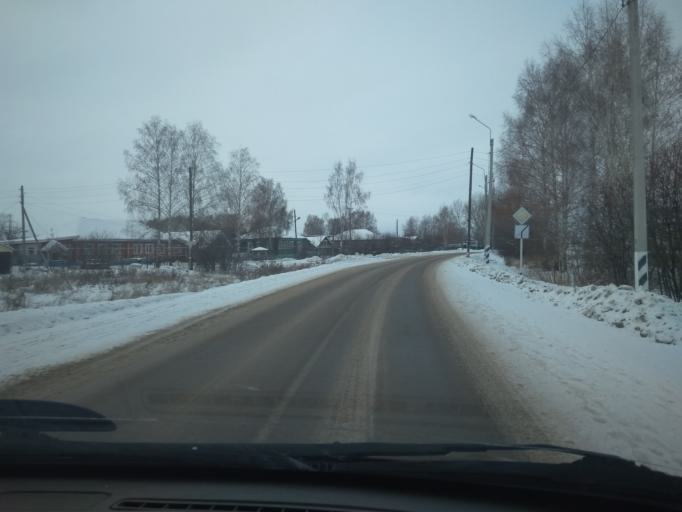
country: RU
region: Mordoviya
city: Ten'gushevo
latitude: 54.7571
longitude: 42.7109
